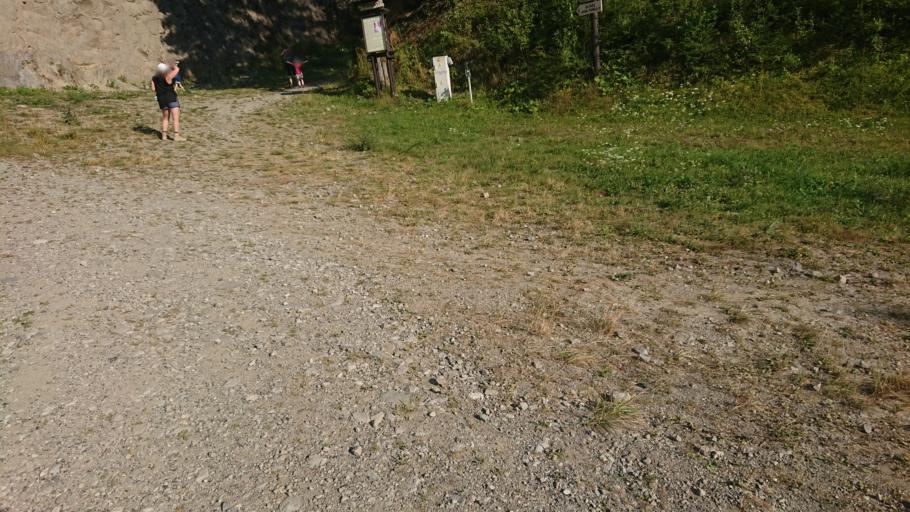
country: PL
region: Lesser Poland Voivodeship
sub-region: Powiat nowotarski
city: Kluszkowce
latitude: 49.4591
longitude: 20.3160
